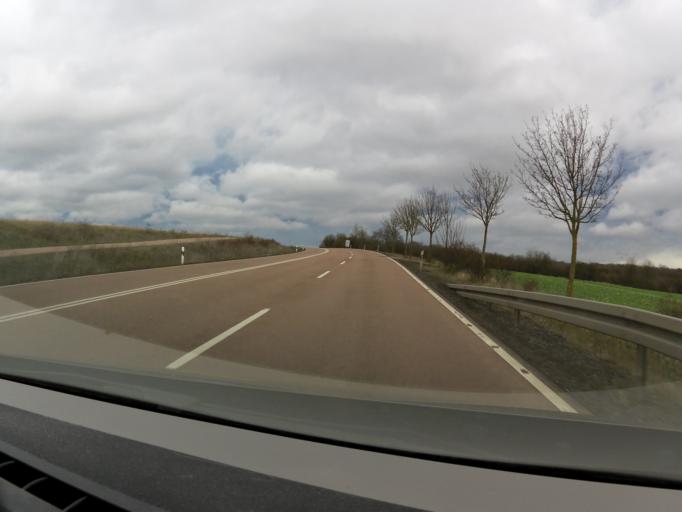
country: DE
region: Saxony-Anhalt
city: Riestedt
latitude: 51.5139
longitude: 11.3755
